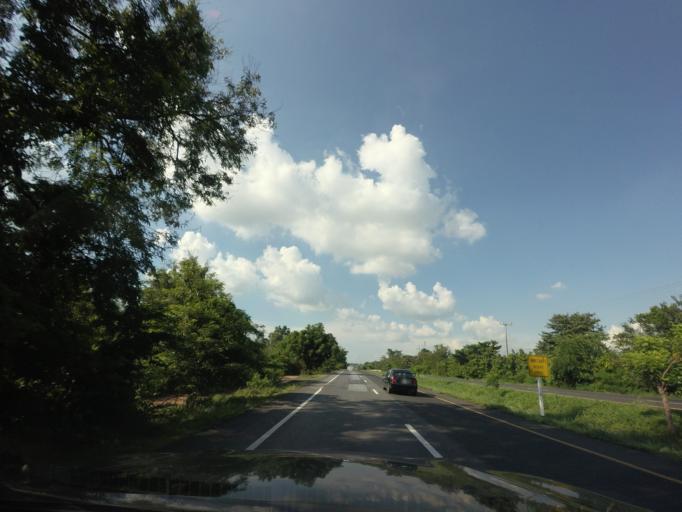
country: TH
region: Nakhon Ratchasima
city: Bua Lai
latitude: 15.6743
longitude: 102.5758
